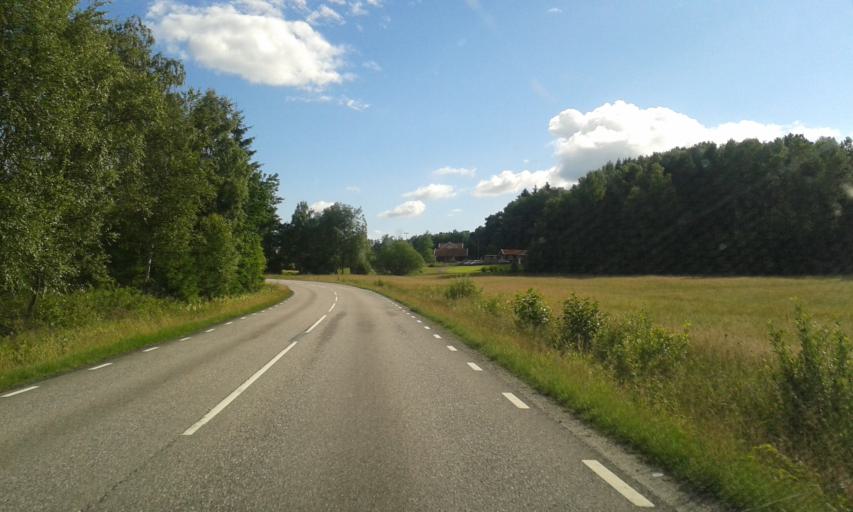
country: SE
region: Vaestra Goetaland
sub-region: Ale Kommun
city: Nodinge-Nol
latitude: 57.9409
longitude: 12.0461
